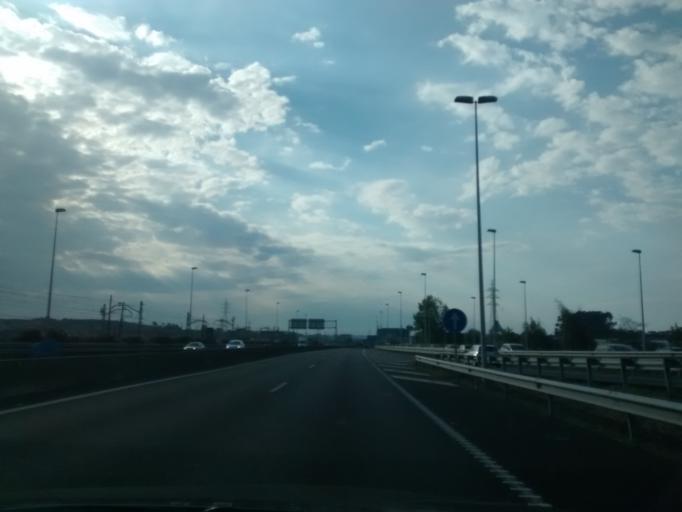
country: ES
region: Cantabria
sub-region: Provincia de Cantabria
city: El Astillero
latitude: 43.4061
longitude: -3.8250
